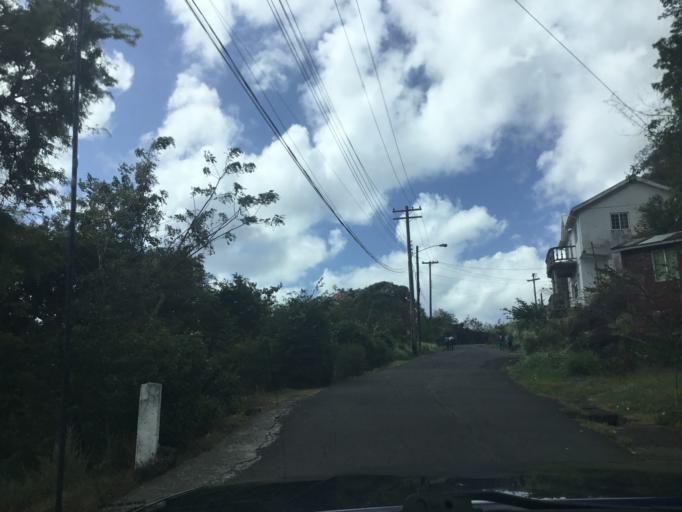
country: VC
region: Saint George
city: Kingstown Park
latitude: 13.1581
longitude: -61.2319
